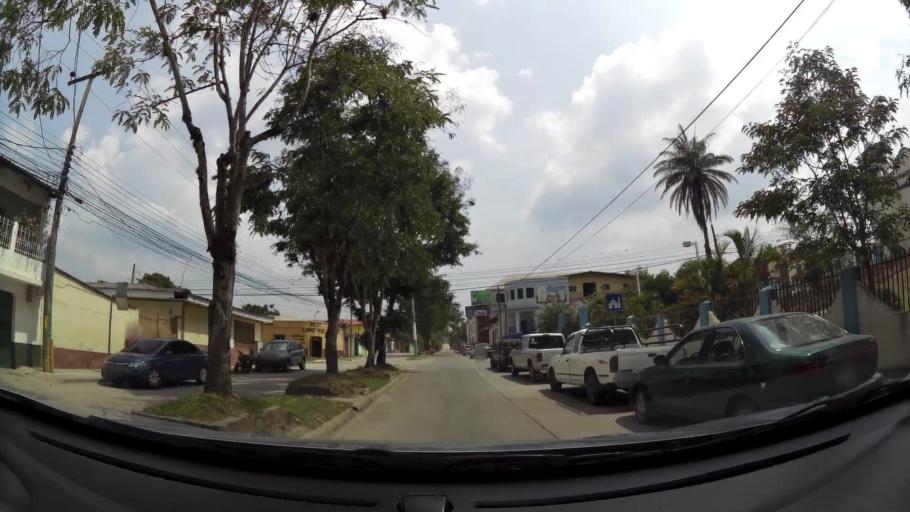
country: HN
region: Comayagua
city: Siguatepeque
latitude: 14.6050
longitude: -87.8306
